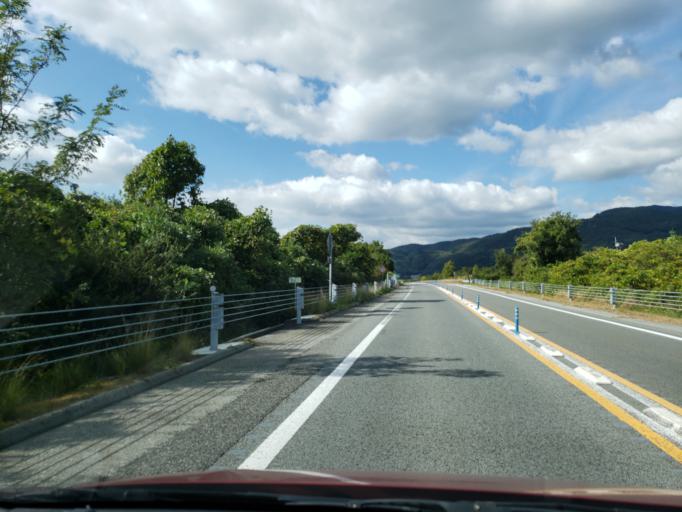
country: JP
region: Tokushima
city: Kamojimacho-jogejima
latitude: 34.1185
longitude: 134.3367
